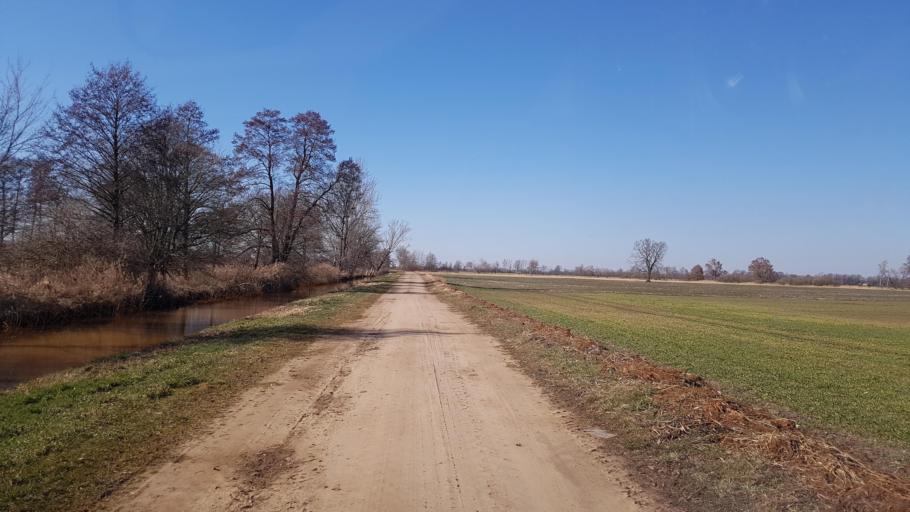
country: DE
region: Brandenburg
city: Hirschfeld
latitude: 51.4150
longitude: 13.6340
